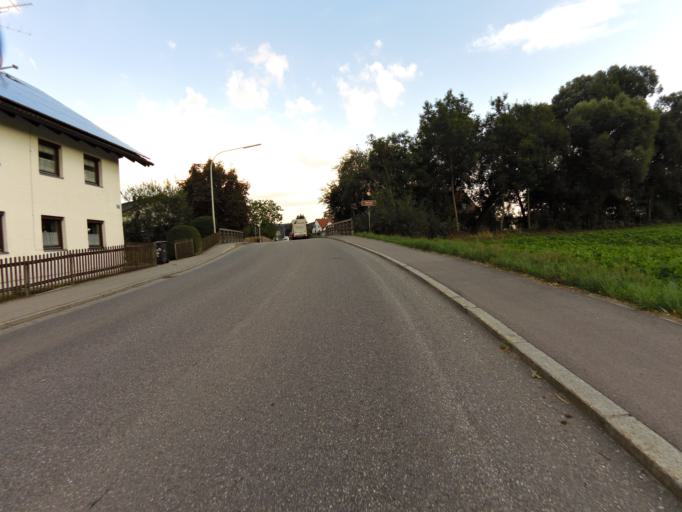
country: DE
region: Bavaria
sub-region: Upper Bavaria
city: Langenpreising
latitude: 48.4589
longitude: 11.9895
